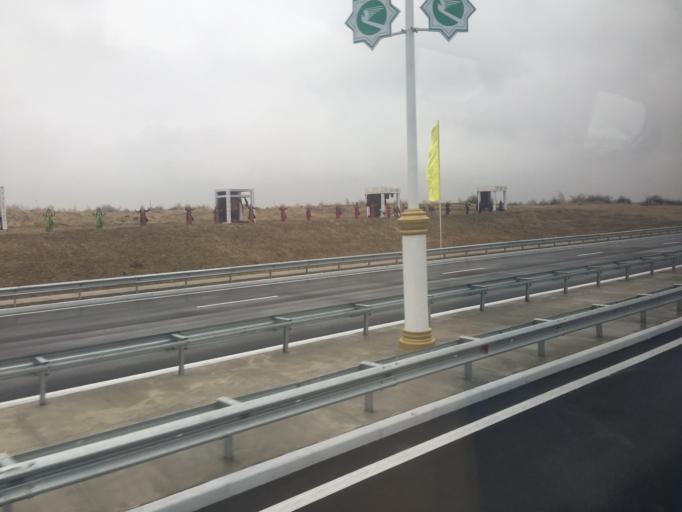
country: TM
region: Lebap
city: Turkmenabat
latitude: 38.9470
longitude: 63.5611
